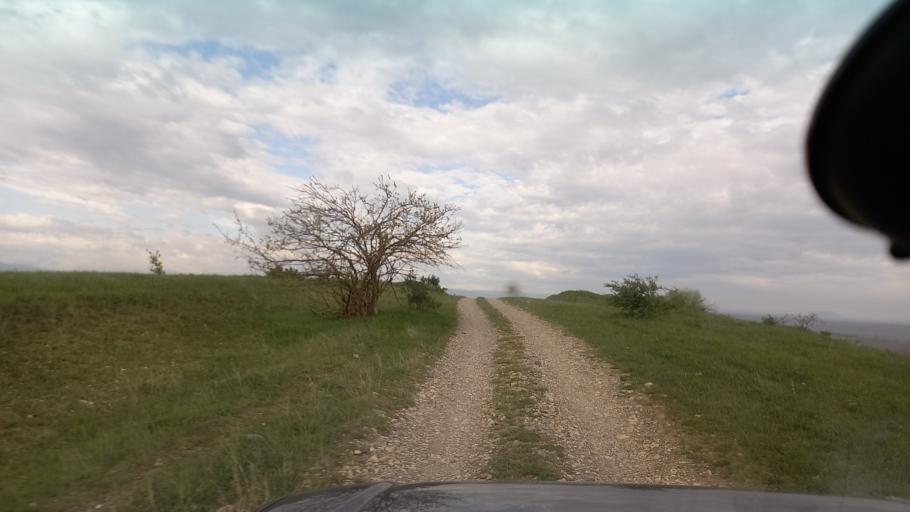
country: RU
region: Kabardino-Balkariya
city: Kuba-Taba
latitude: 43.8051
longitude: 43.4026
